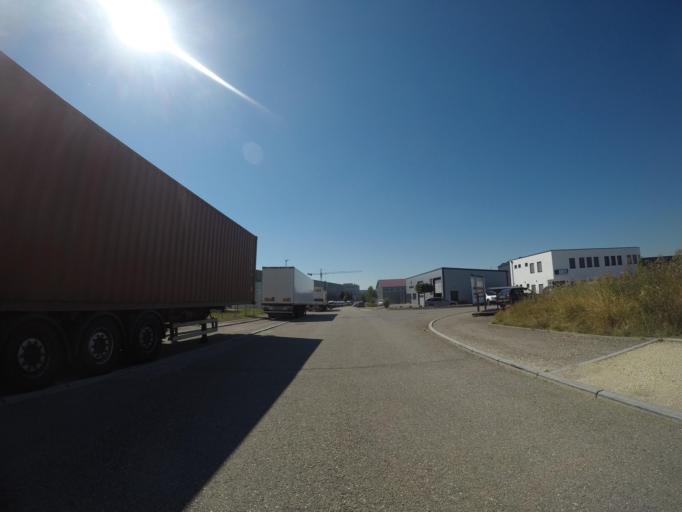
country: DE
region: Baden-Wuerttemberg
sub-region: Tuebingen Region
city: Dornstadt
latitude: 48.4632
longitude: 9.9660
